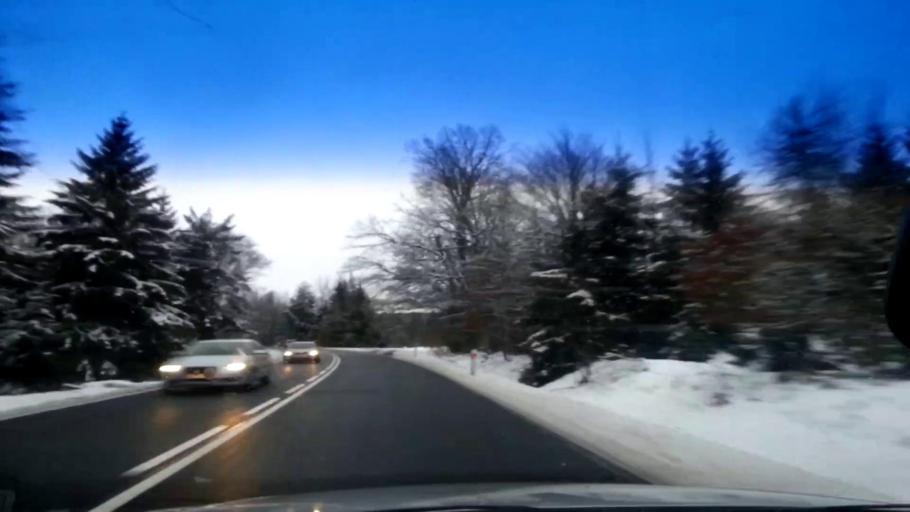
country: CZ
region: Karlovarsky
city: Hazlov
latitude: 50.1870
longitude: 12.2406
